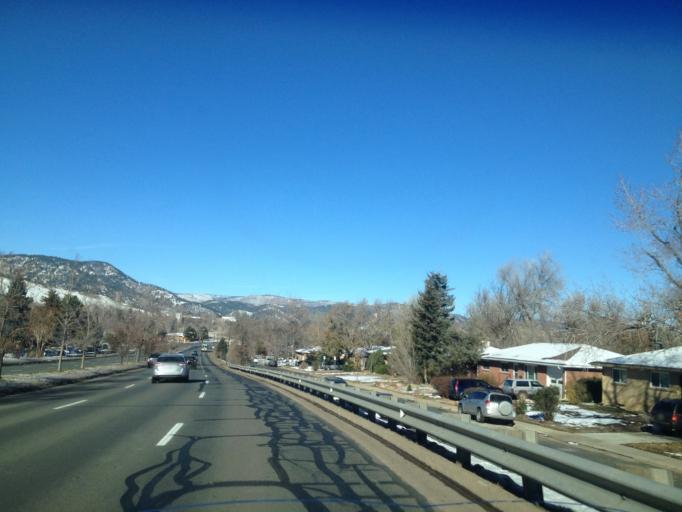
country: US
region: Colorado
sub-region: Boulder County
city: Boulder
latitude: 39.9873
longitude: -105.2516
